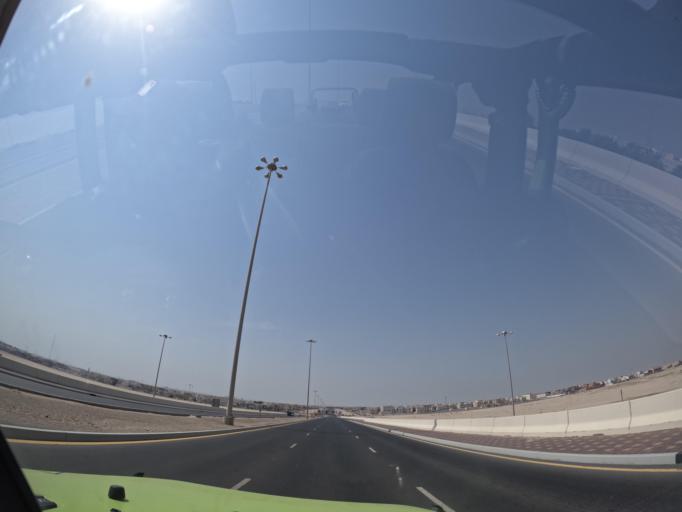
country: AE
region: Abu Dhabi
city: Abu Dhabi
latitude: 24.3393
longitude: 54.6381
